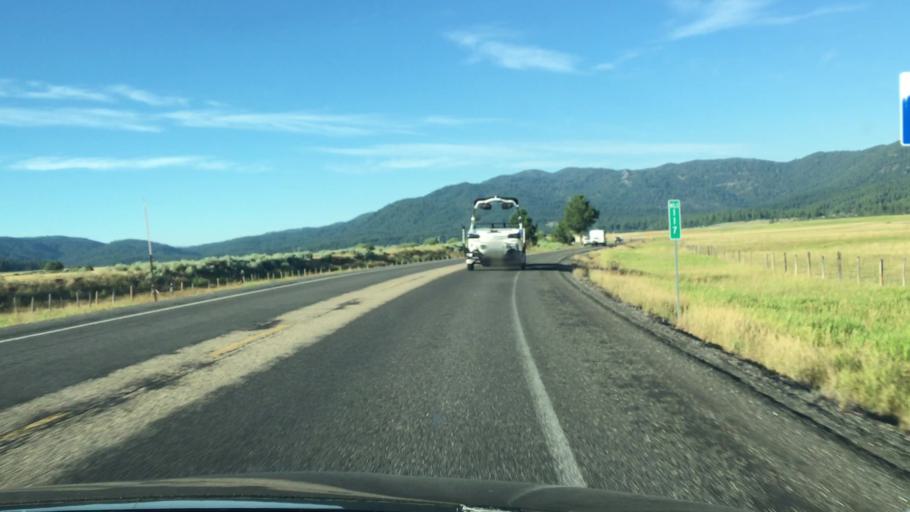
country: US
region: Idaho
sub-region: Valley County
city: Cascade
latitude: 44.5386
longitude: -116.0319
